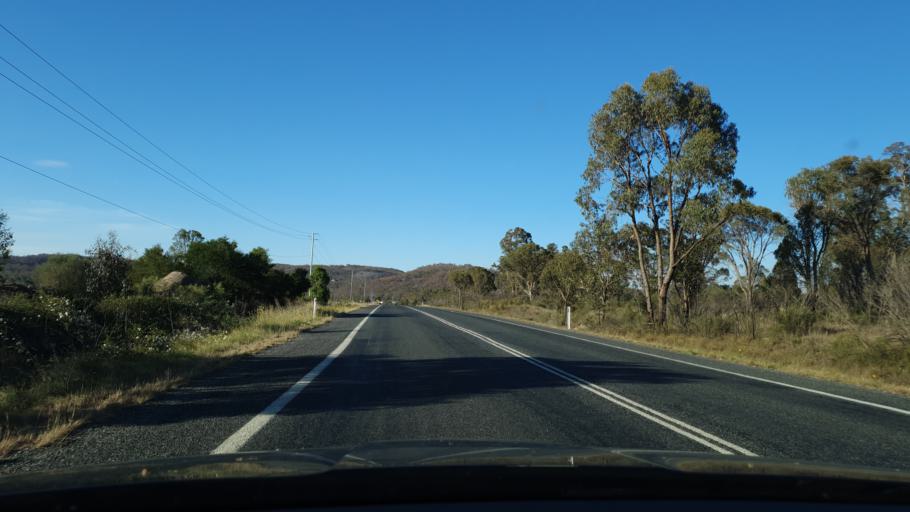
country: AU
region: Queensland
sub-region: Southern Downs
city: Stanthorpe
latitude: -28.6614
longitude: 151.9162
